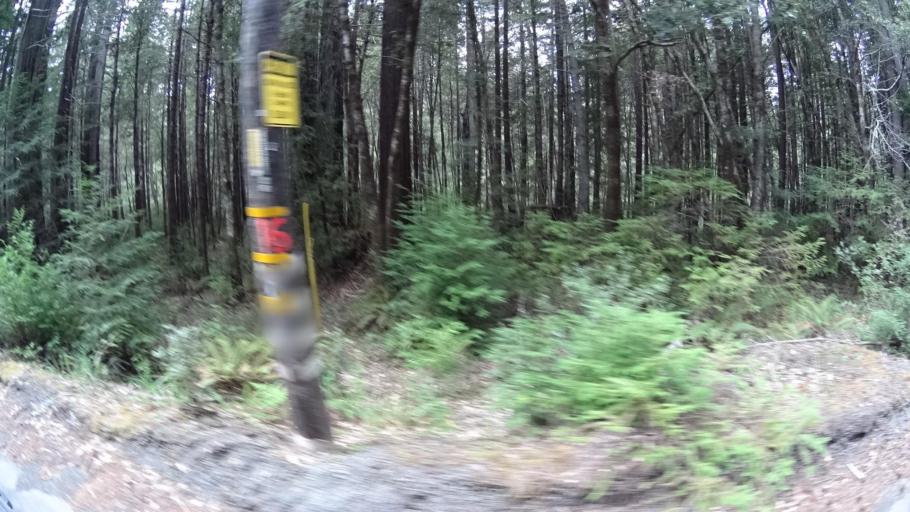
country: US
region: California
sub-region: Humboldt County
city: Redway
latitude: 39.9987
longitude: -123.9278
